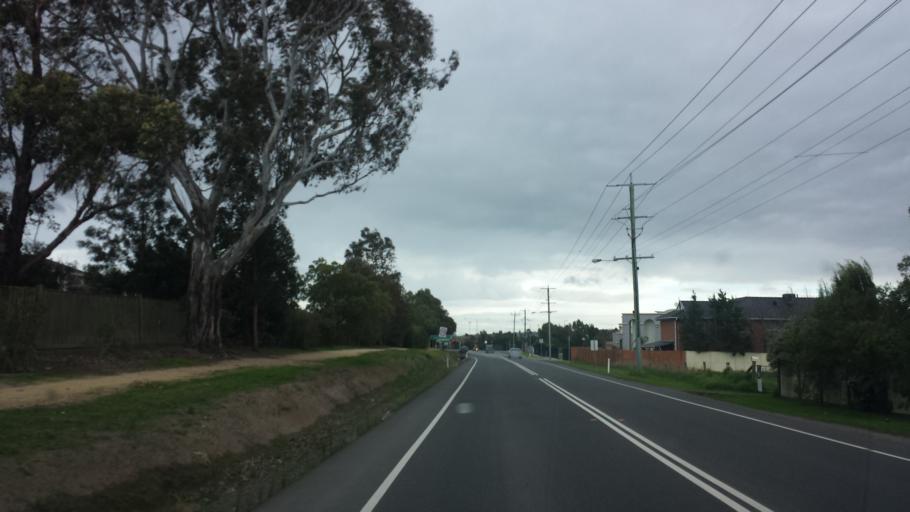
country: AU
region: Victoria
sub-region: Casey
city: Endeavour Hills
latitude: -37.9896
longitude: 145.2804
